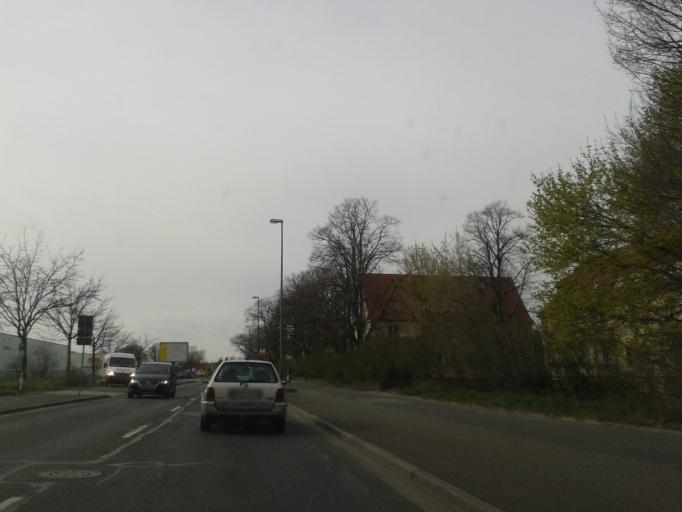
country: DE
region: Saxony
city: Radebeul
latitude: 51.0862
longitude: 13.6825
